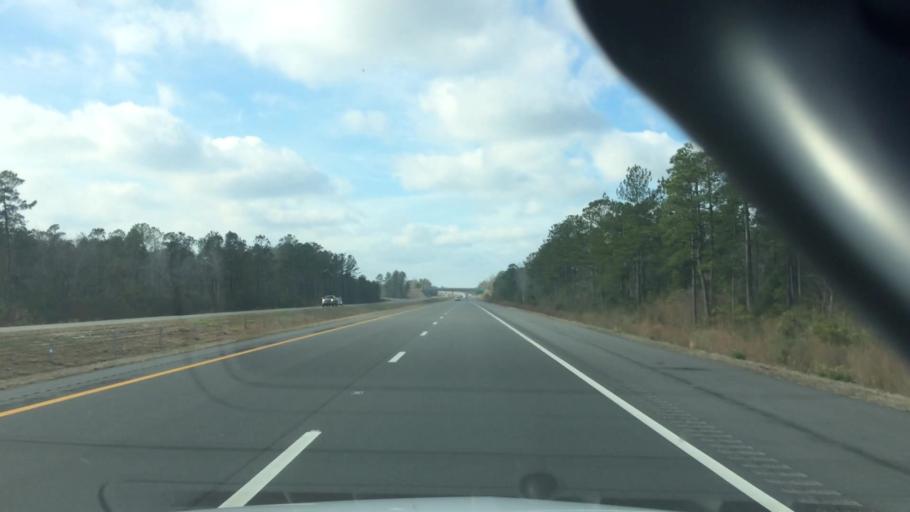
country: US
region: North Carolina
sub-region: Brunswick County
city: Leland
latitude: 34.2758
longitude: -78.0407
